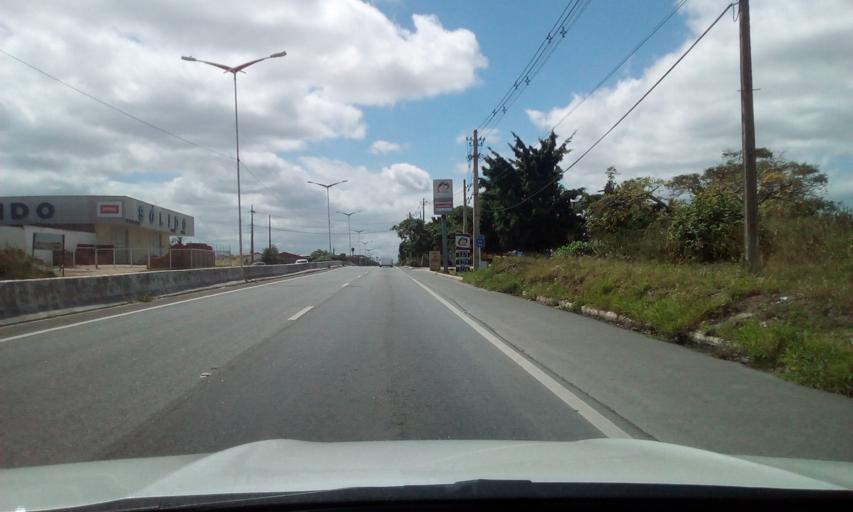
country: BR
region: Paraiba
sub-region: Campina Grande
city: Campina Grande
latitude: -7.2447
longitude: -35.8526
